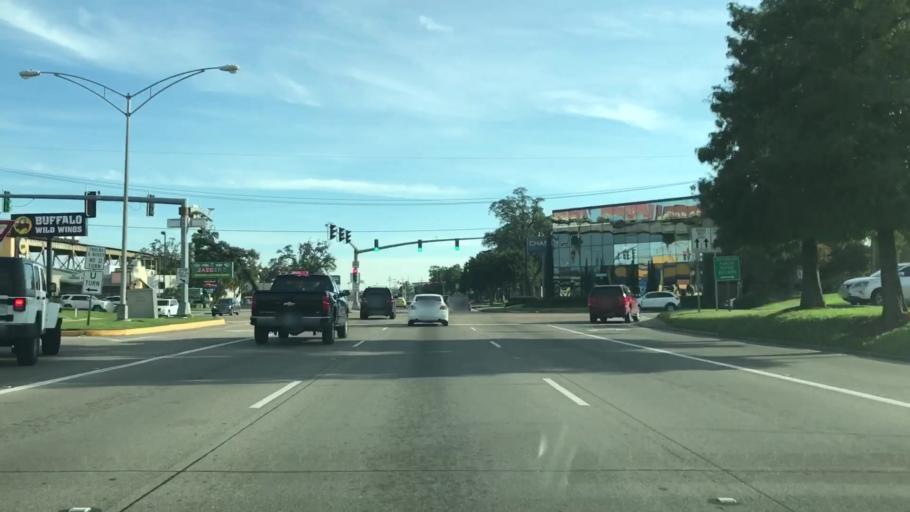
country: US
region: Louisiana
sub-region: Jefferson Parish
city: Elmwood
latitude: 29.9588
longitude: -90.1834
